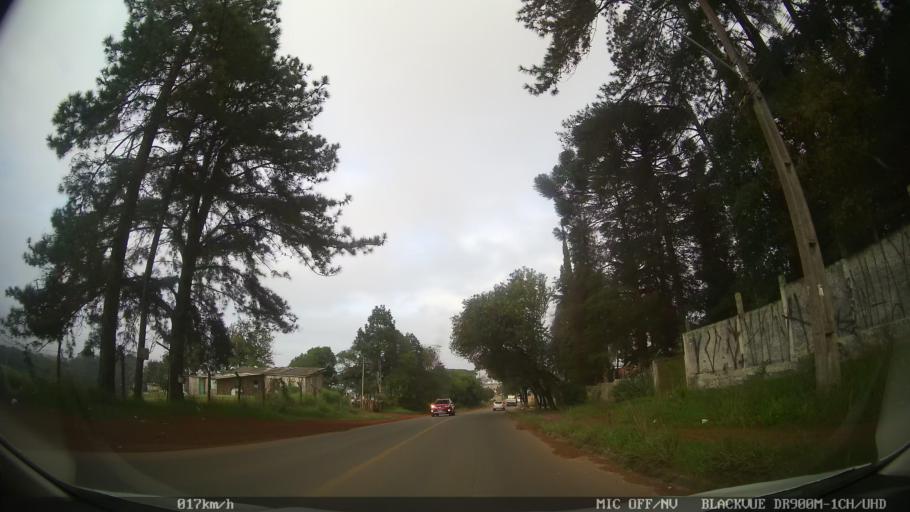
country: BR
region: Parana
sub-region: Almirante Tamandare
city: Almirante Tamandare
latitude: -25.3705
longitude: -49.3287
